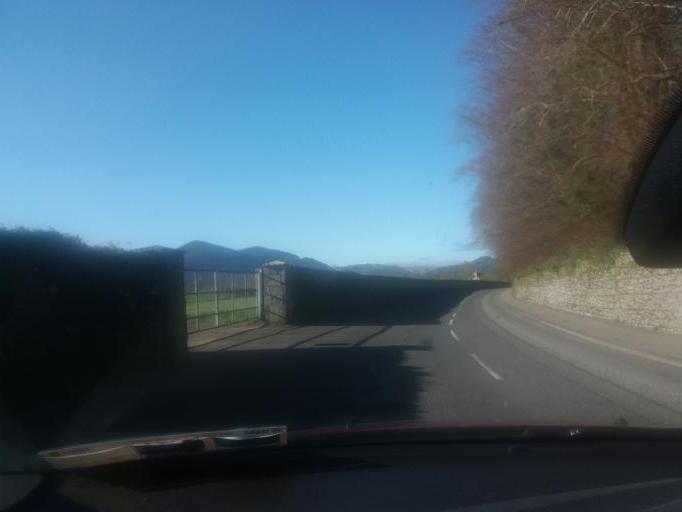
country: IE
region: Munster
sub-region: Ciarrai
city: Cill Airne
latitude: 52.0503
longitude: -9.5175
